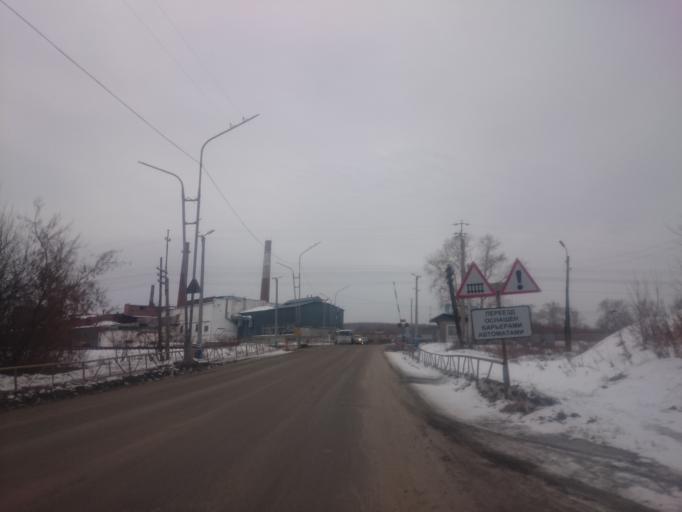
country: RU
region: Sverdlovsk
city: Irbit
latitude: 57.6664
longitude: 63.0597
